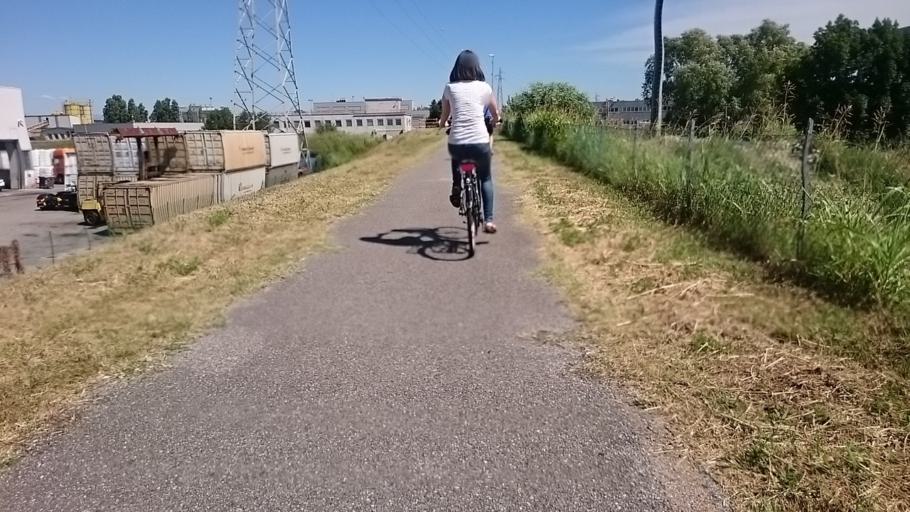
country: IT
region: Veneto
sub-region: Provincia di Padova
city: Noventa
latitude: 45.4058
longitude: 11.9370
